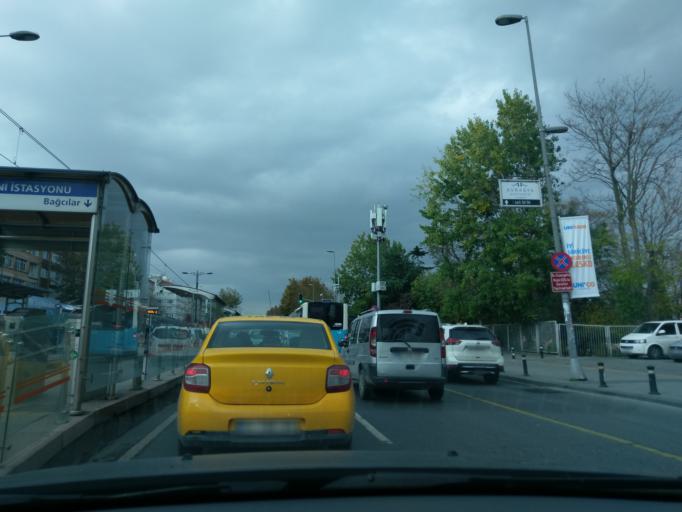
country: TR
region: Istanbul
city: Istanbul
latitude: 41.0152
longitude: 28.9337
